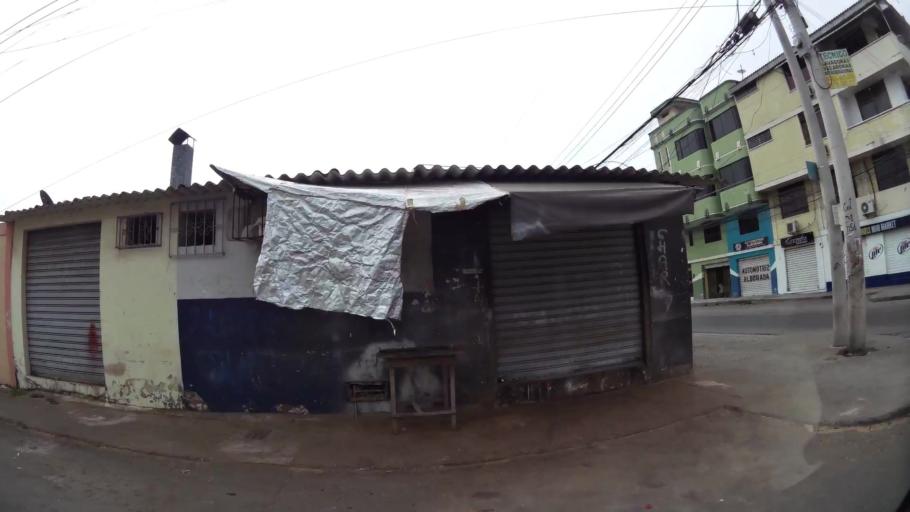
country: EC
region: Guayas
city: Eloy Alfaro
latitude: -2.1366
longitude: -79.8948
